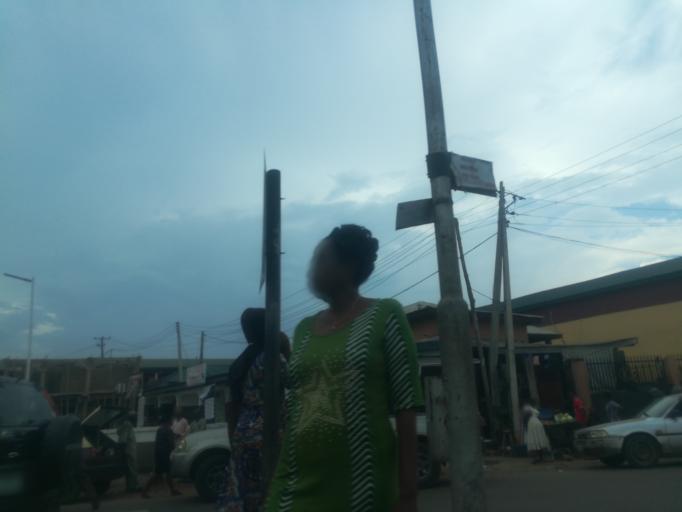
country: NG
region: Oyo
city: Ibadan
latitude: 7.4316
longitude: 3.9128
